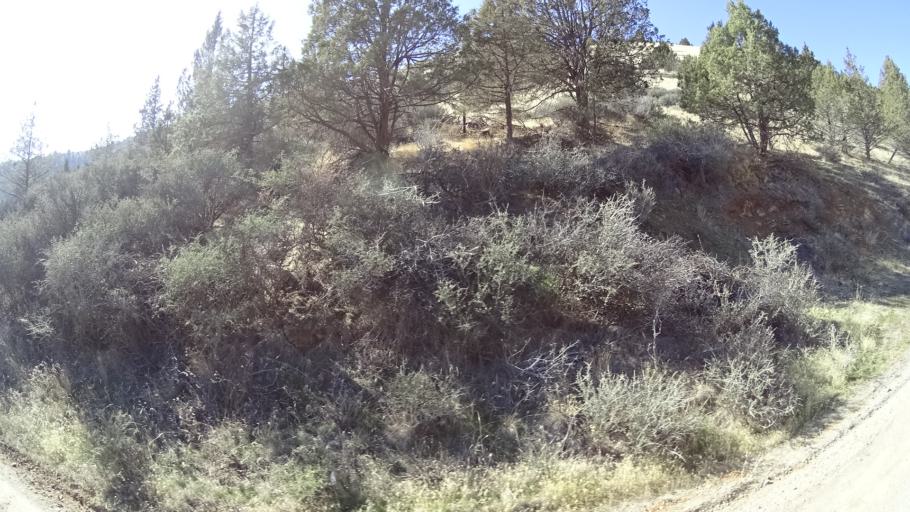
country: US
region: California
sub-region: Siskiyou County
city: Yreka
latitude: 41.7865
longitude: -122.6027
